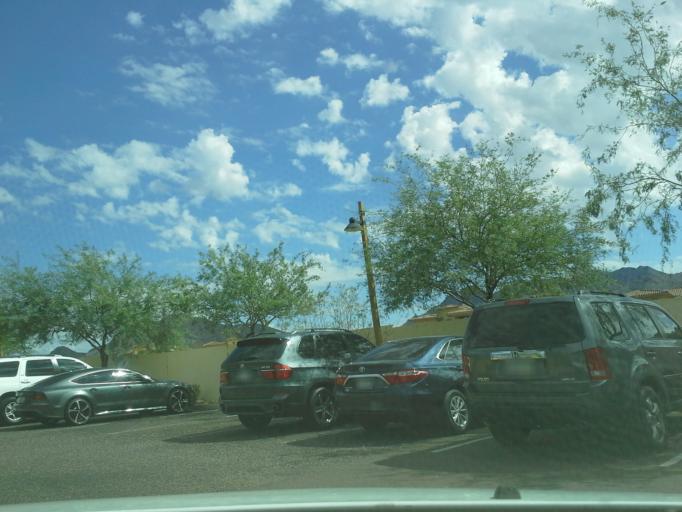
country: US
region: Arizona
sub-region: Maricopa County
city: Paradise Valley
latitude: 33.6554
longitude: -111.8649
